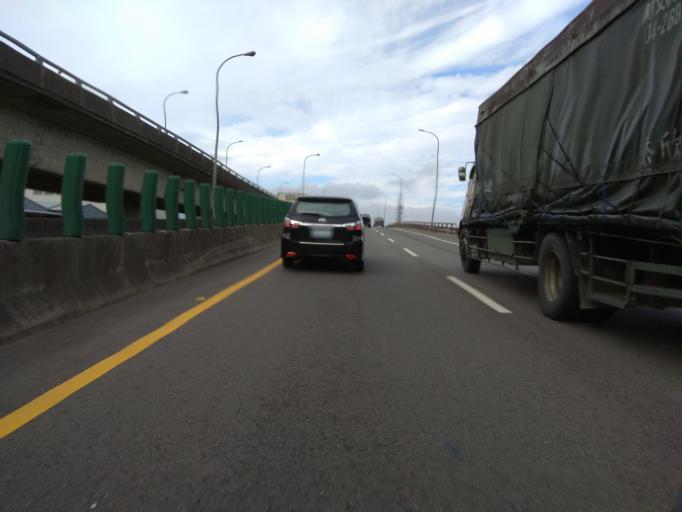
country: TW
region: Taiwan
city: Daxi
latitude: 24.8983
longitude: 121.2596
